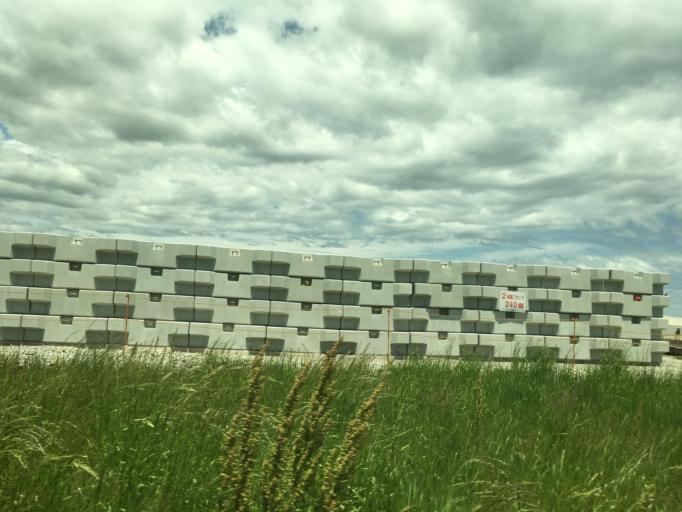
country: JP
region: Fukushima
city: Namie
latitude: 37.4830
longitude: 141.0392
